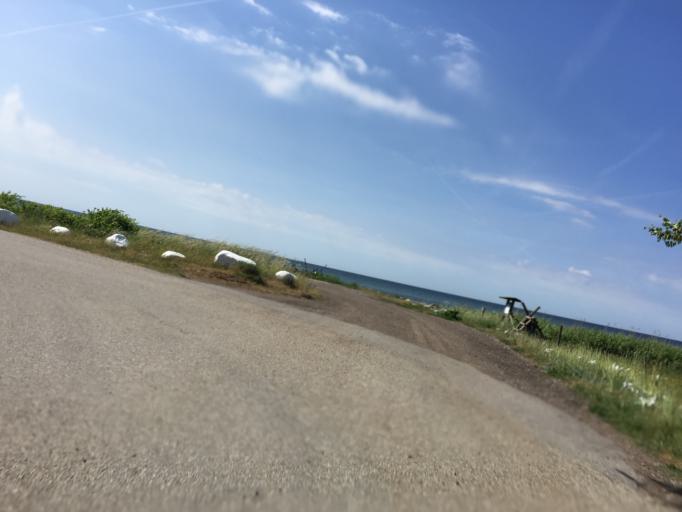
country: SE
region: Skane
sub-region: Trelleborgs Kommun
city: Trelleborg
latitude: 55.3572
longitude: 13.2275
